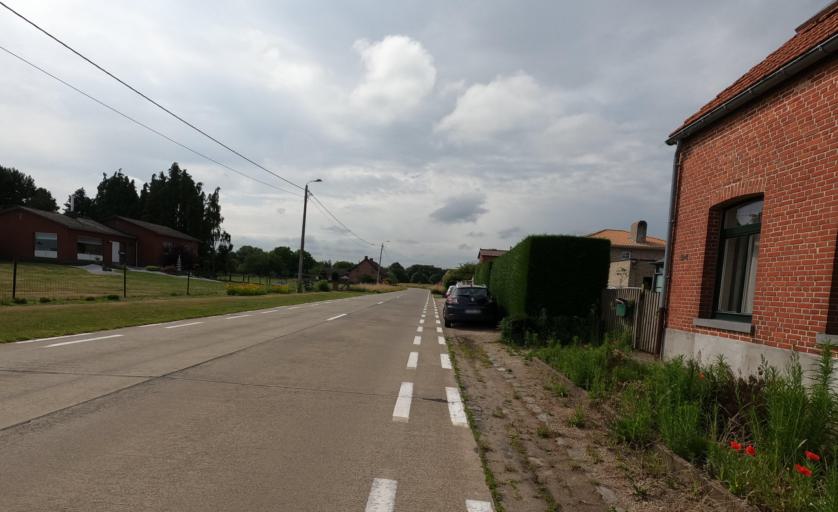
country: BE
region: Flanders
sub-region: Provincie Antwerpen
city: Heist-op-den-Berg
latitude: 51.1144
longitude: 4.7222
